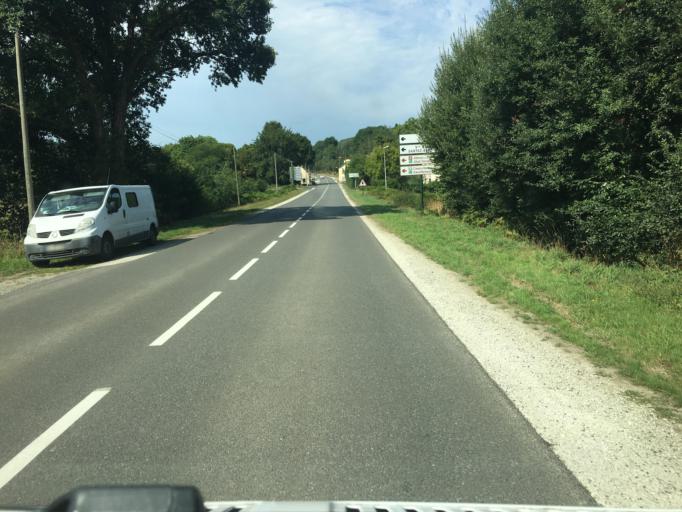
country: FR
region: Brittany
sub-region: Departement des Cotes-d'Armor
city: Gouarec
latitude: 48.2145
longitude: -3.1246
